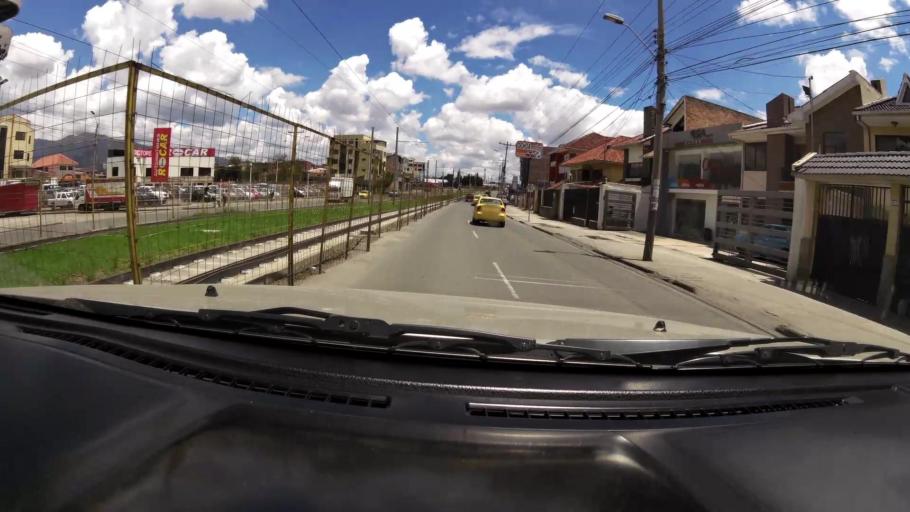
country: EC
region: Azuay
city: Cuenca
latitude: -2.9052
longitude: -79.0324
